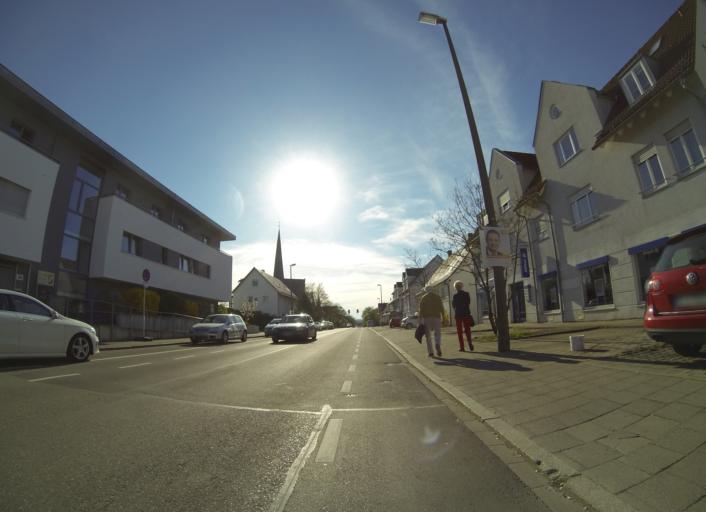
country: DE
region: Baden-Wuerttemberg
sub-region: Tuebingen Region
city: Ulm
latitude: 48.3605
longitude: 9.9860
